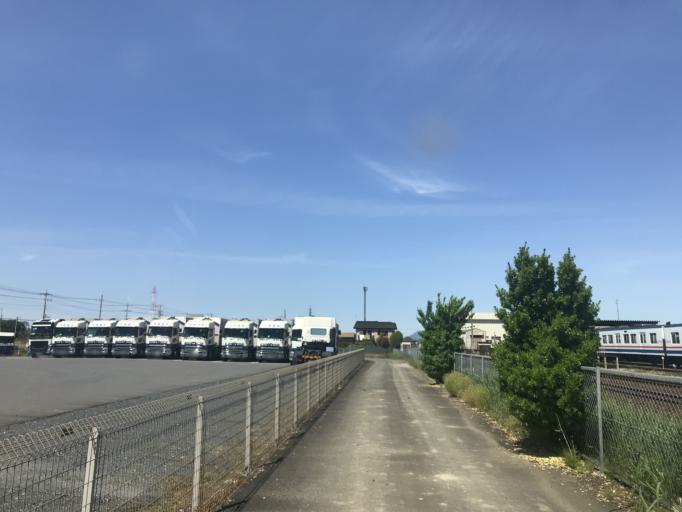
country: JP
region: Ibaraki
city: Mitsukaido
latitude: 36.0045
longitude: 139.9804
